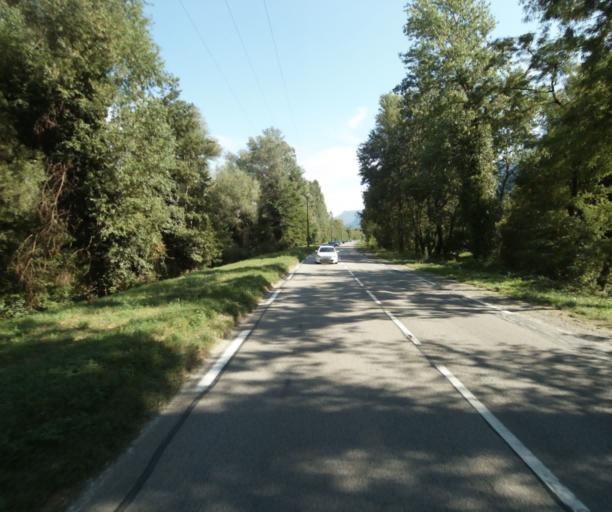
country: FR
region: Rhone-Alpes
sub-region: Departement de l'Isere
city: Voreppe
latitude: 45.2933
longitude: 5.6147
